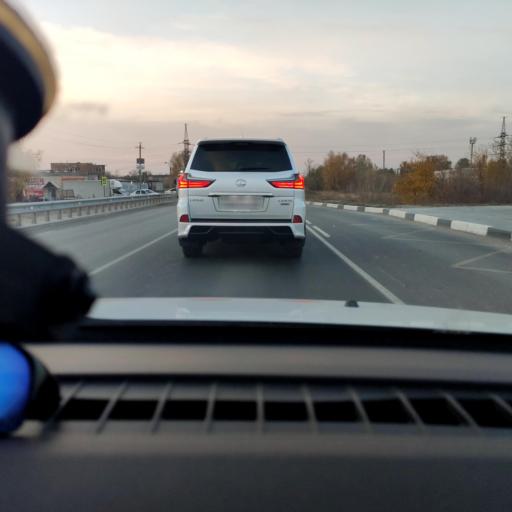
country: RU
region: Samara
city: Samara
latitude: 53.1286
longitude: 50.1104
